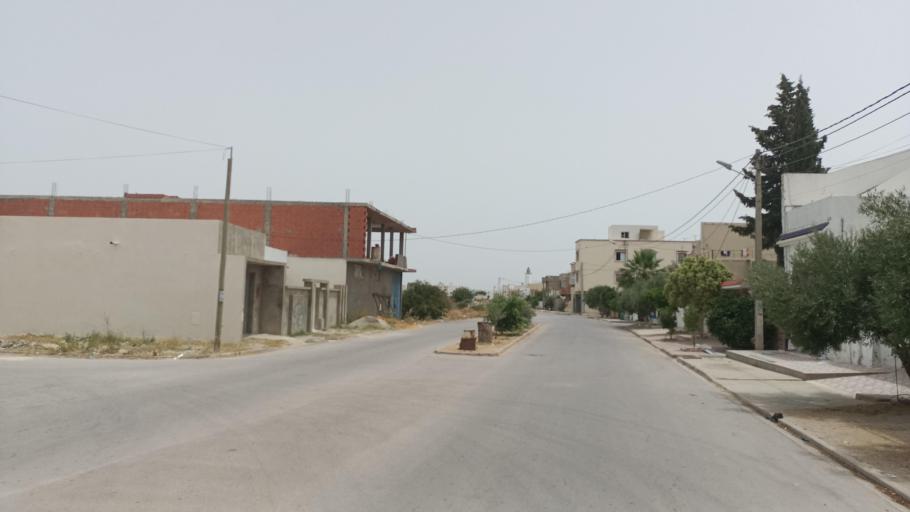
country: TN
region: Nabul
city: Manzil Bu Zalafah
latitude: 36.6984
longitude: 10.4818
